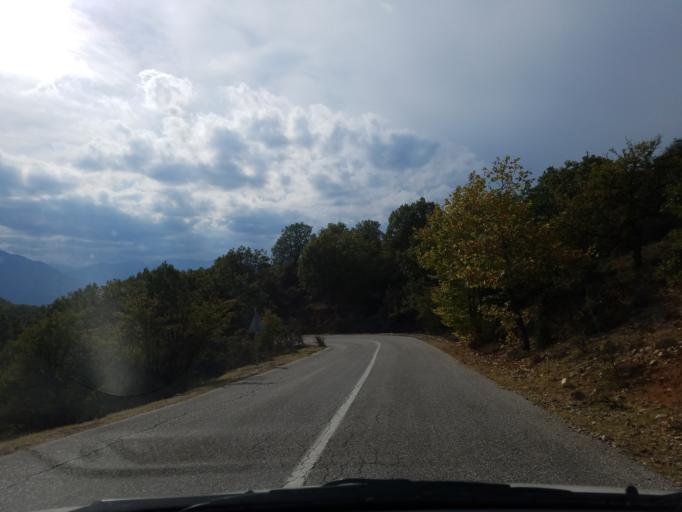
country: GR
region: Thessaly
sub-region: Trikala
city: Kastraki
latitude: 39.7302
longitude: 21.6499
